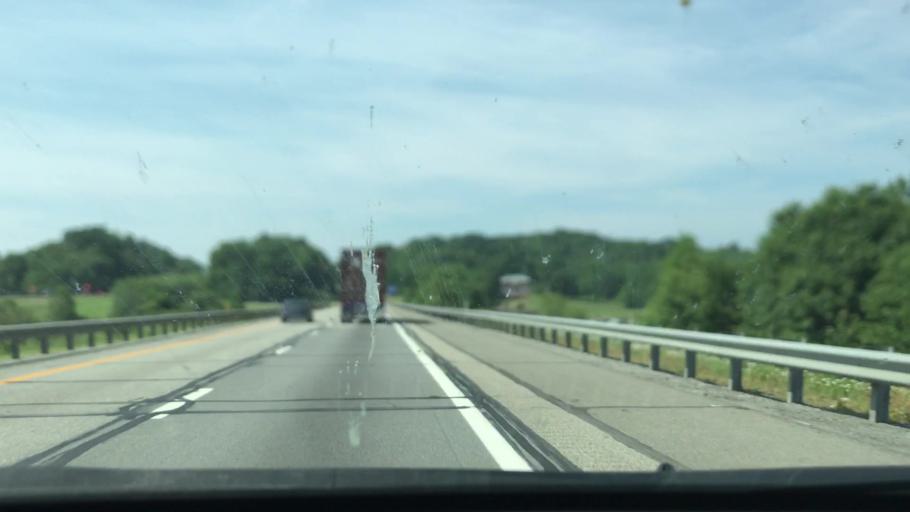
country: US
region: West Virginia
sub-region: Raleigh County
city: Shady Spring
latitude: 37.6270
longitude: -81.1161
